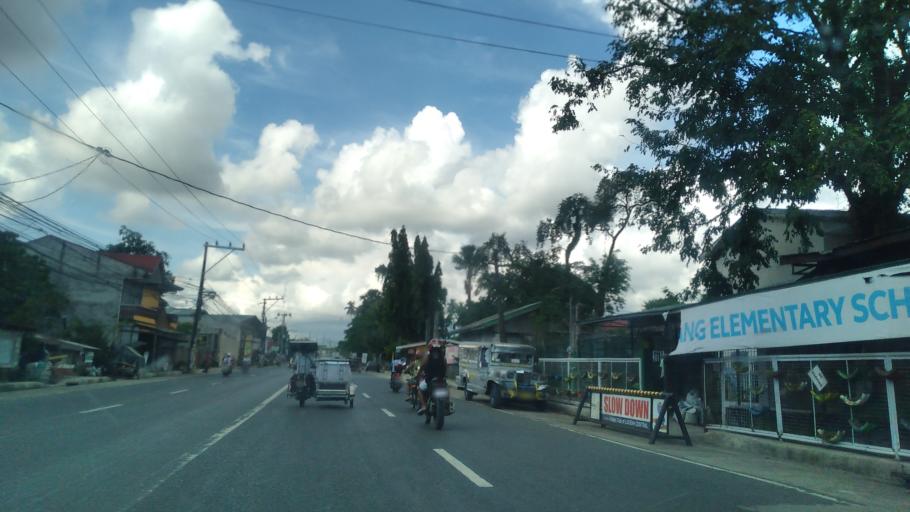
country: PH
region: Calabarzon
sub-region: Province of Quezon
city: Isabang
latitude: 13.9496
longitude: 121.5812
